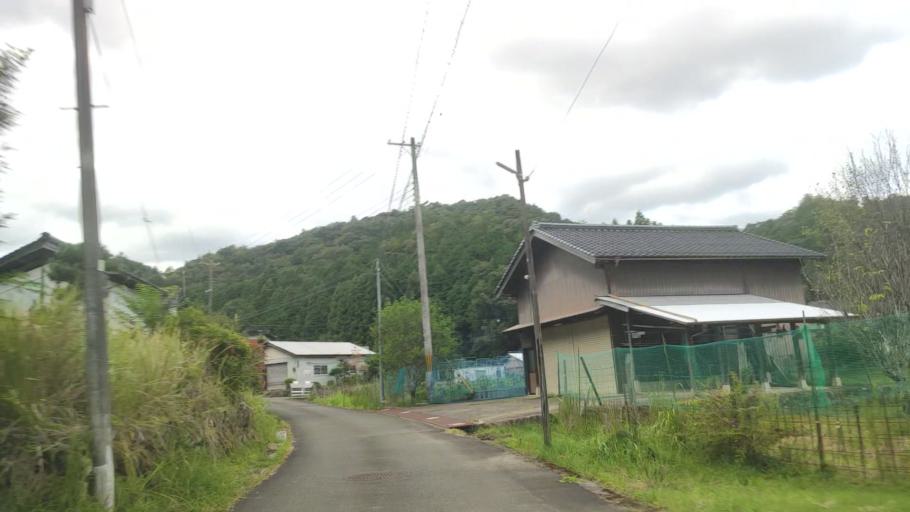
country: JP
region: Hyogo
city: Toyooka
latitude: 35.6004
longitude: 134.8799
